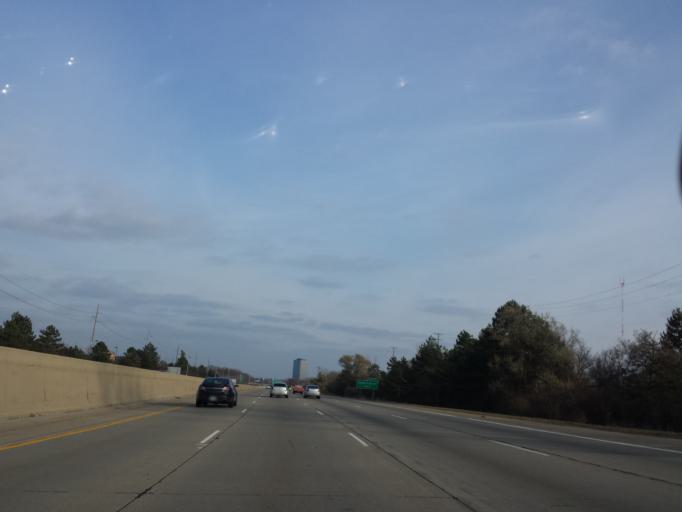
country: US
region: Michigan
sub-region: Oakland County
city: Franklin
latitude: 42.4905
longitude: -83.3293
